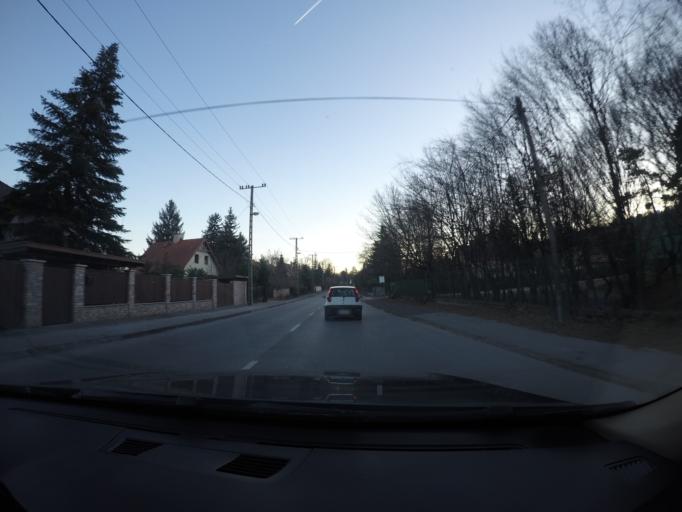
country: HU
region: Pest
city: Leanyfalu
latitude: 47.7009
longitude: 19.0885
